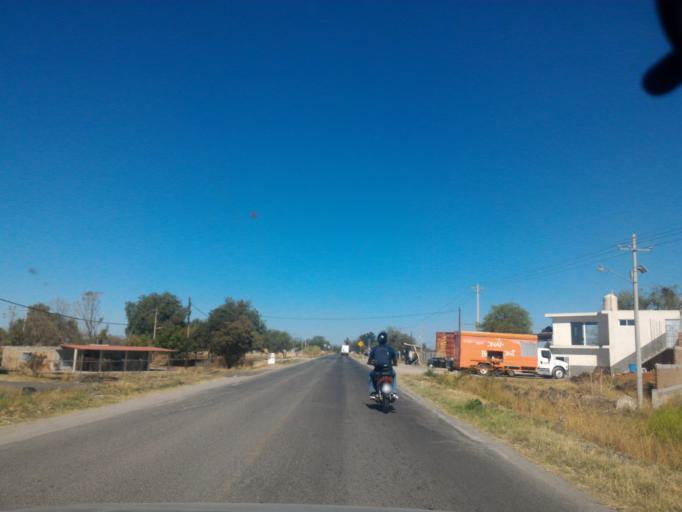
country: MX
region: Guanajuato
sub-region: San Francisco del Rincon
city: San Roque de Montes
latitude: 20.9970
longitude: -101.8131
